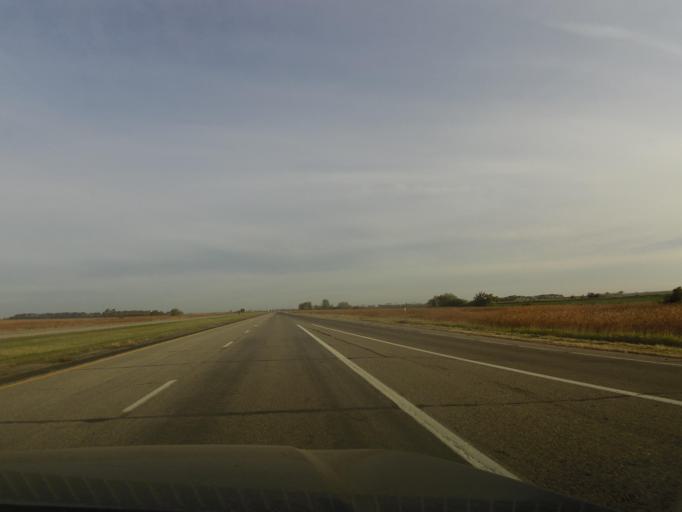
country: US
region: Minnesota
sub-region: Kittson County
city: Hallock
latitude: 48.6320
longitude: -97.1820
